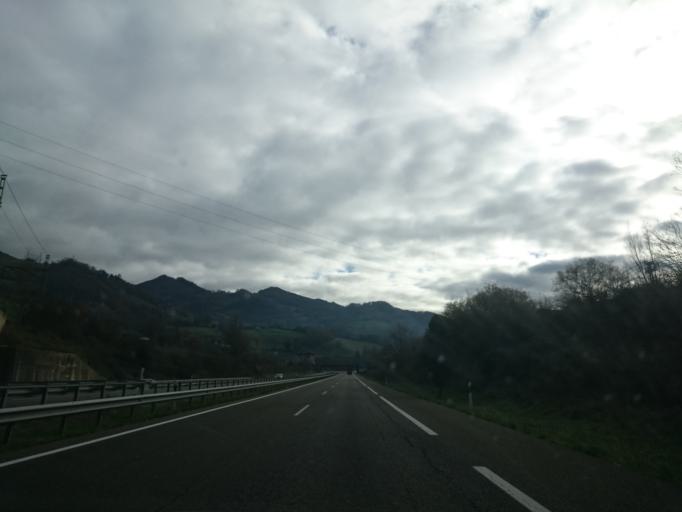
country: ES
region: Asturias
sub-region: Province of Asturias
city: Pola de Lena
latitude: 43.1332
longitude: -5.8196
